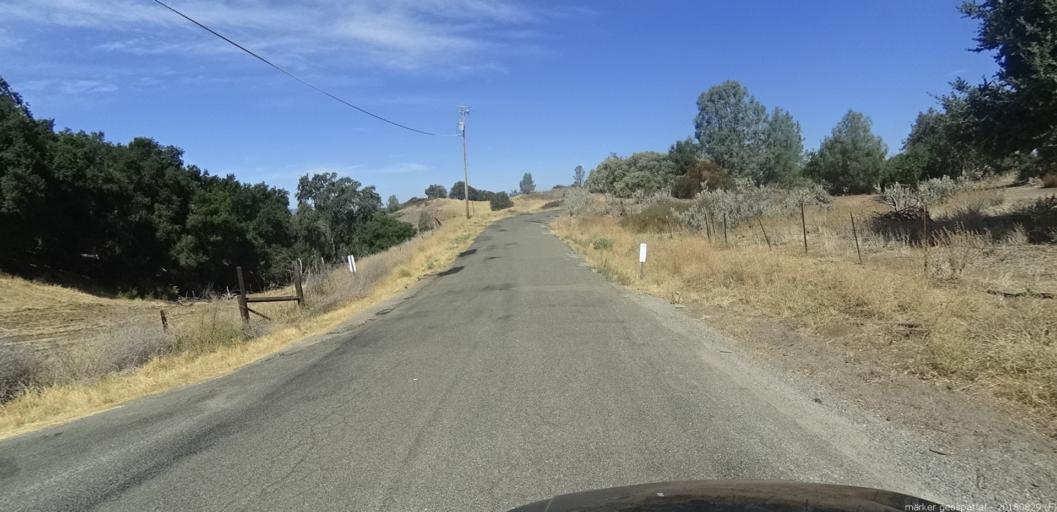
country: US
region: California
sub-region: San Luis Obispo County
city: Lake Nacimiento
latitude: 35.8181
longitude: -121.0570
